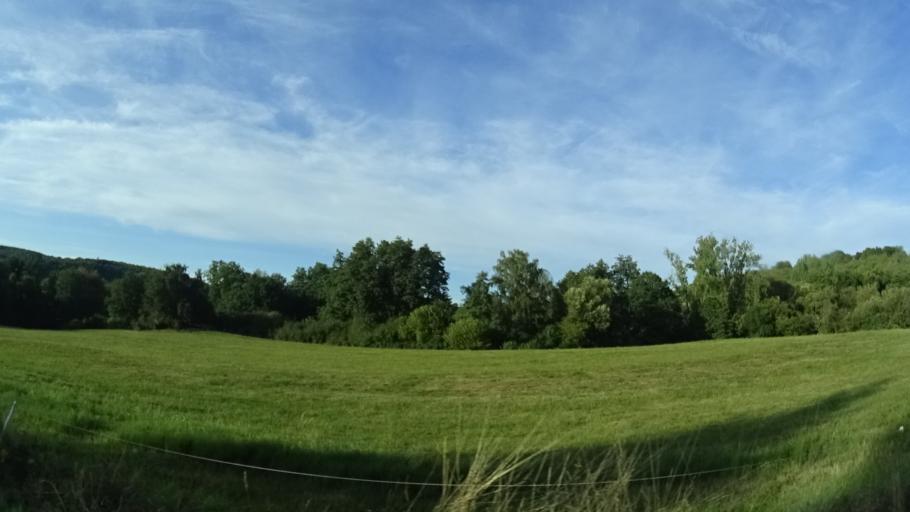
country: DE
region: Hesse
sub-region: Regierungsbezirk Darmstadt
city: Birstein
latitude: 50.3151
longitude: 9.3183
